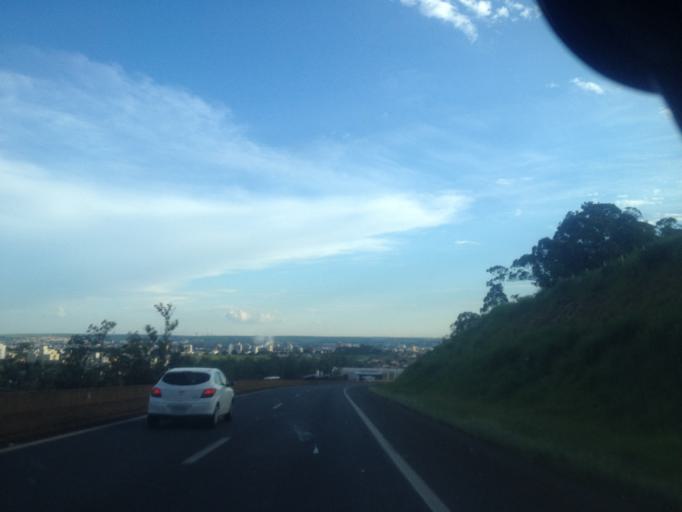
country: BR
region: Sao Paulo
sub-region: Araras
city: Araras
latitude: -22.3305
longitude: -47.3893
